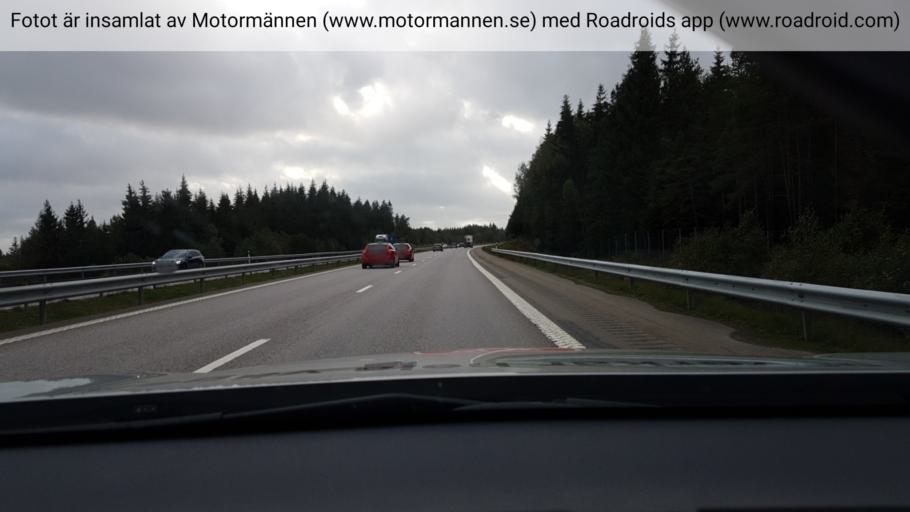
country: SE
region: Vaestra Goetaland
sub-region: Boras Kommun
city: Sandared
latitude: 57.6825
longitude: 12.7388
